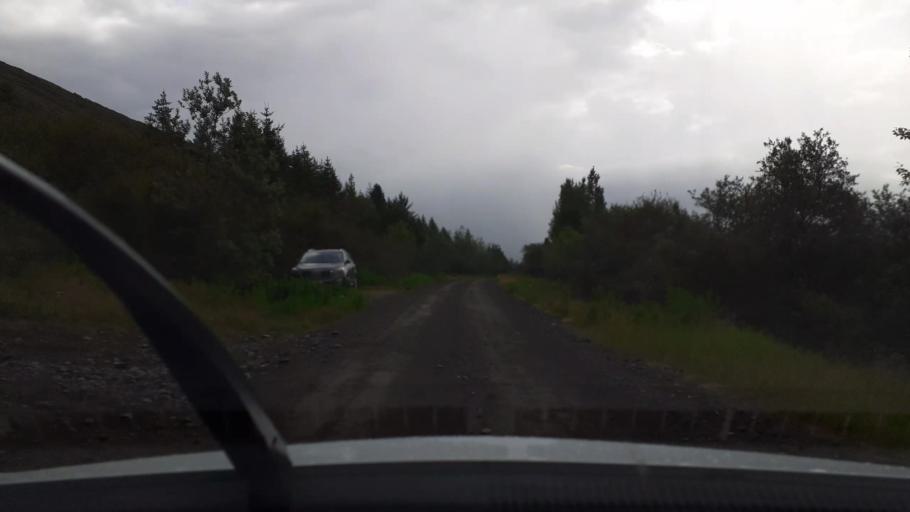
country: IS
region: Capital Region
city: Mosfellsbaer
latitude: 64.4951
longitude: -21.3522
